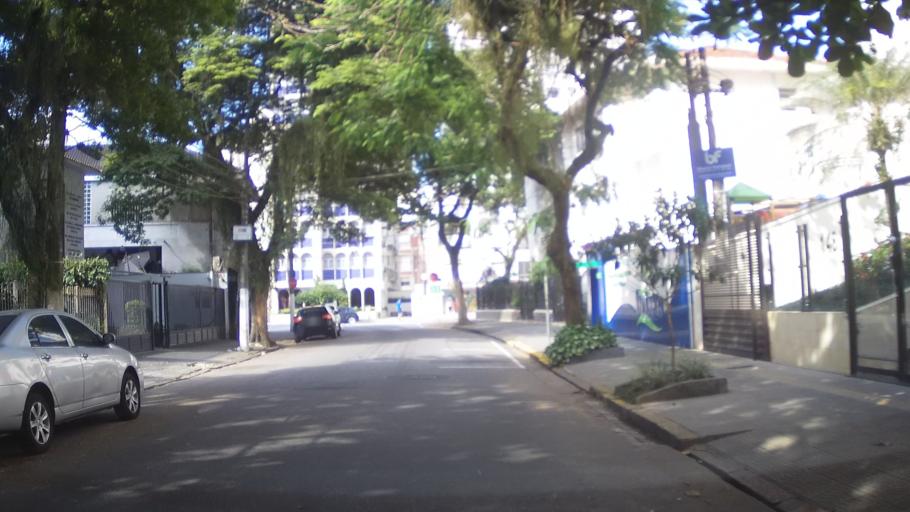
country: BR
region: Sao Paulo
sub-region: Santos
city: Santos
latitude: -23.9676
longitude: -46.3267
